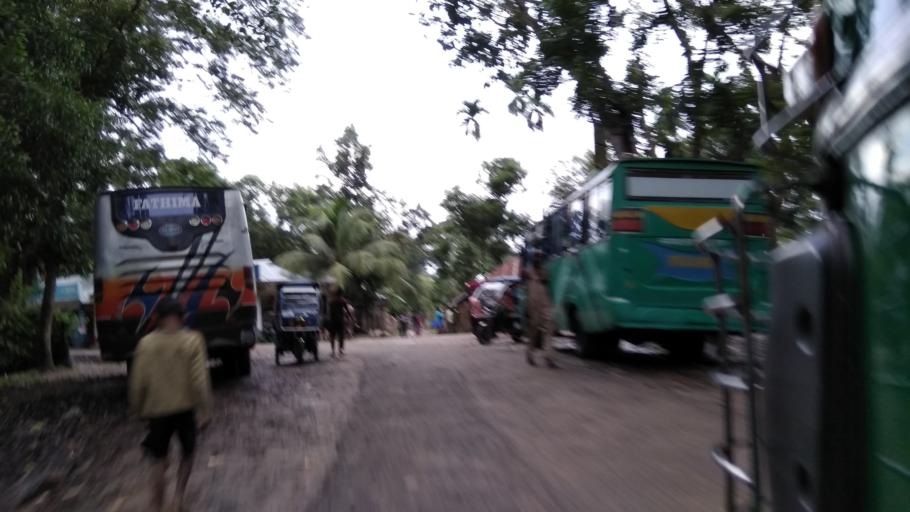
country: IN
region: Tripura
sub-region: Dhalai
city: Kamalpur
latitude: 24.2074
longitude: 91.8649
